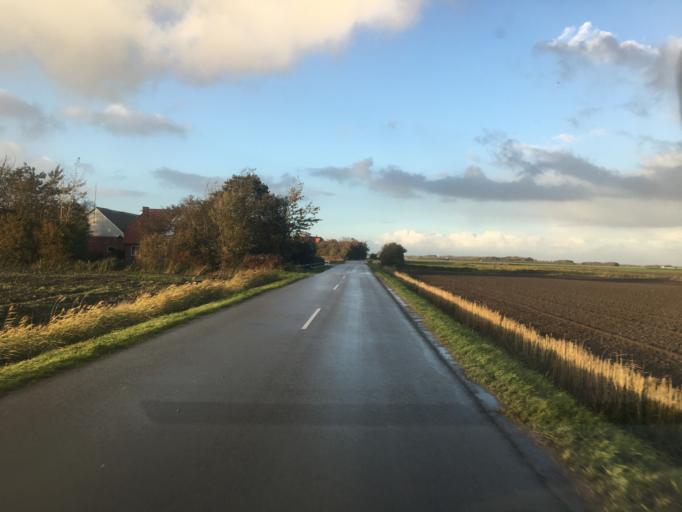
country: DE
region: Schleswig-Holstein
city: Aventoft
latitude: 54.9103
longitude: 8.7690
